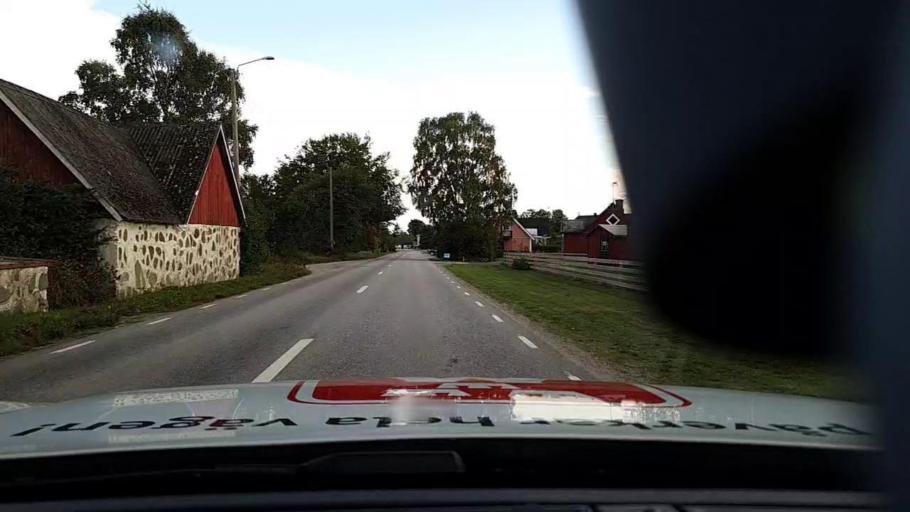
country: SE
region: Blekinge
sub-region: Solvesborgs Kommun
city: Soelvesborg
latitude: 56.0181
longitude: 14.7172
